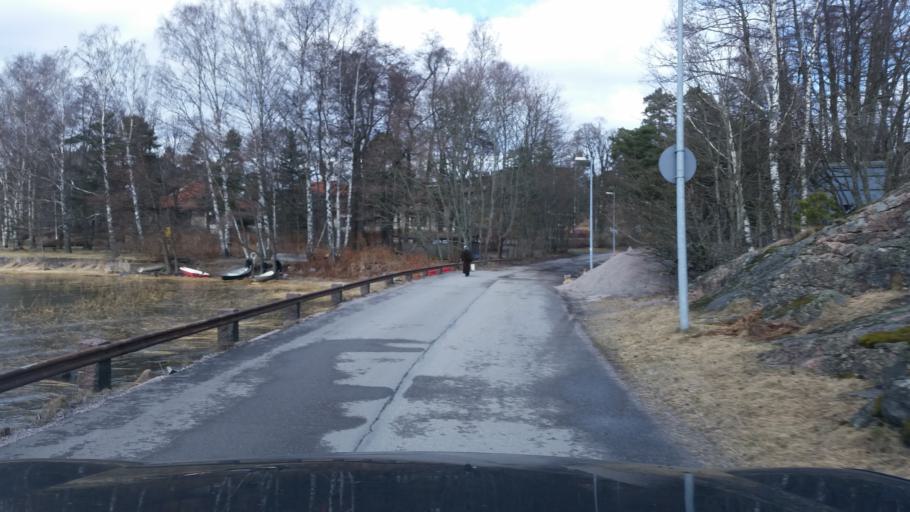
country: FI
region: Uusimaa
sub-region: Helsinki
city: Teekkarikylae
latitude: 60.1899
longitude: 24.8734
